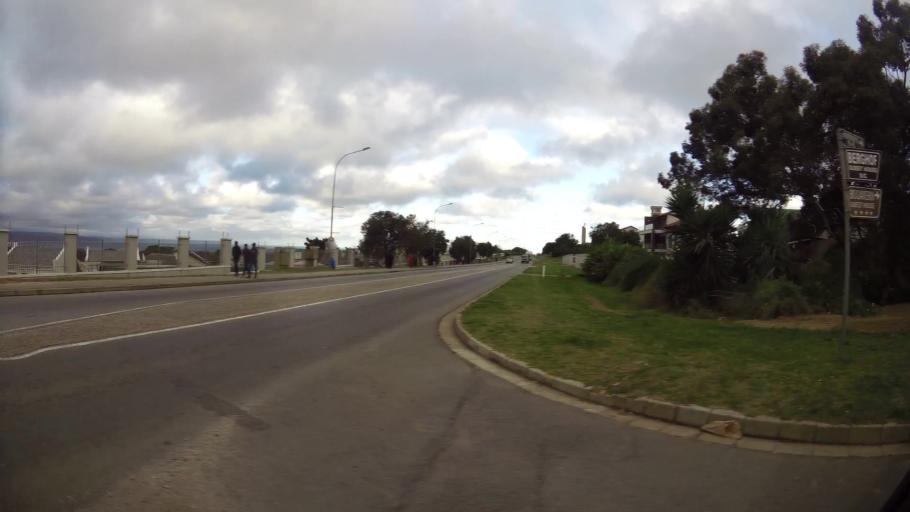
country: ZA
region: Western Cape
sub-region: Eden District Municipality
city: Plettenberg Bay
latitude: -34.0527
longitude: 23.3634
